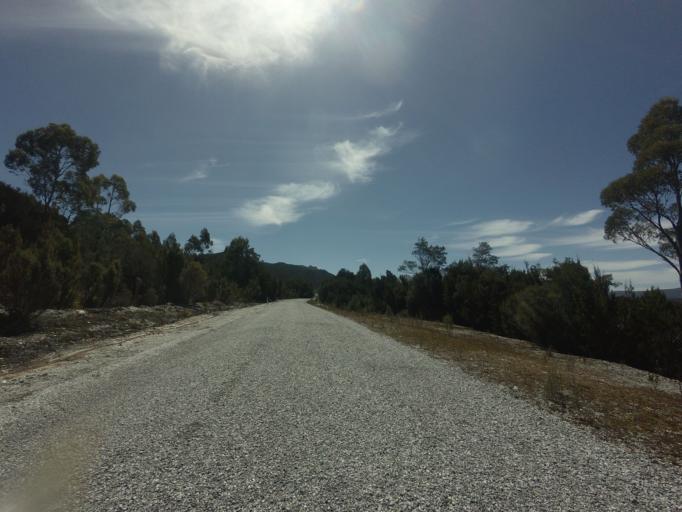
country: AU
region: Tasmania
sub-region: West Coast
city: Queenstown
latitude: -42.7336
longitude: 145.9788
